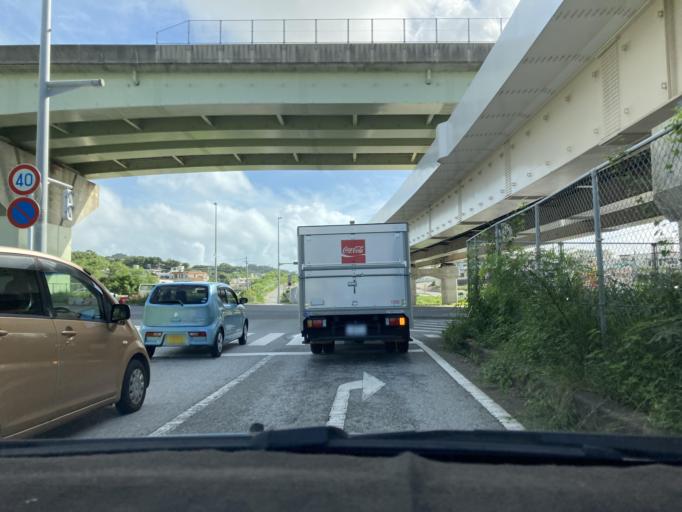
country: JP
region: Okinawa
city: Naha-shi
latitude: 26.2023
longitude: 127.7385
